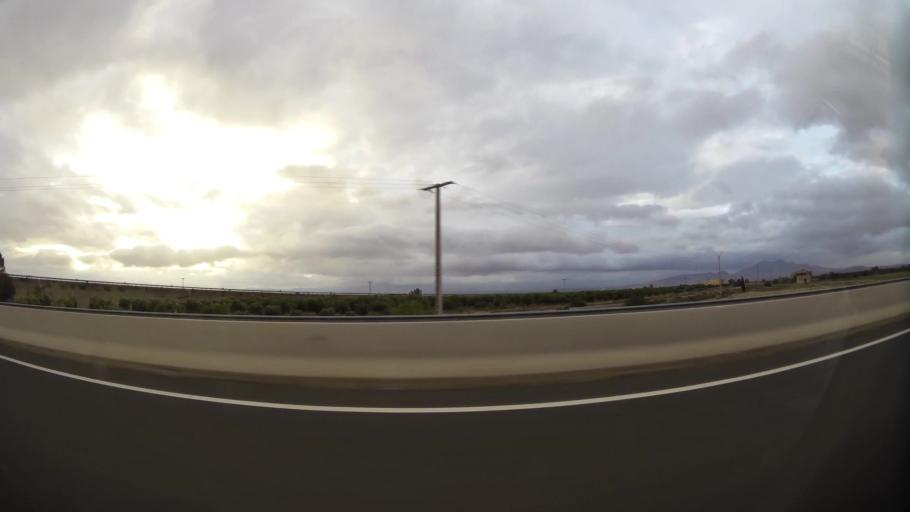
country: MA
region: Taza-Al Hoceima-Taounate
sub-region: Taza
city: Guercif
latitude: 34.3561
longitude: -3.3040
